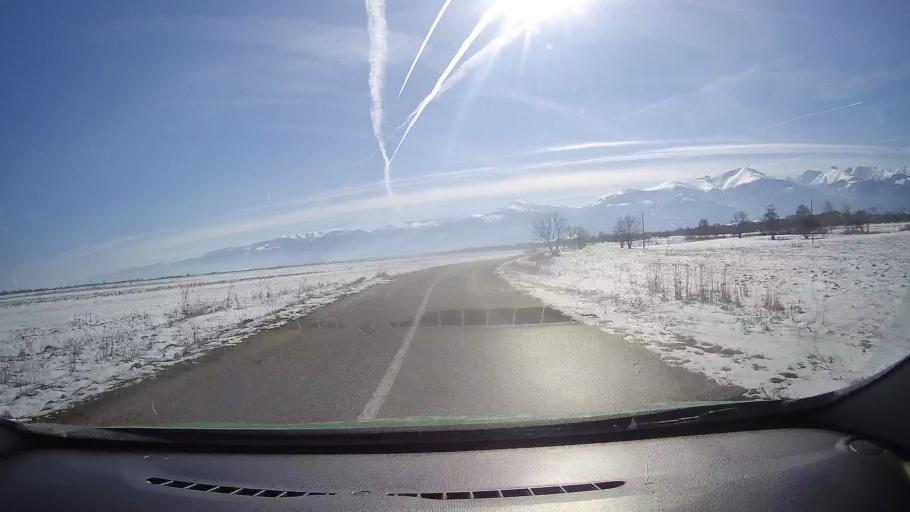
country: RO
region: Brasov
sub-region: Comuna Sambata de Sus
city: Sambata de Sus
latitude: 45.7460
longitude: 24.8426
